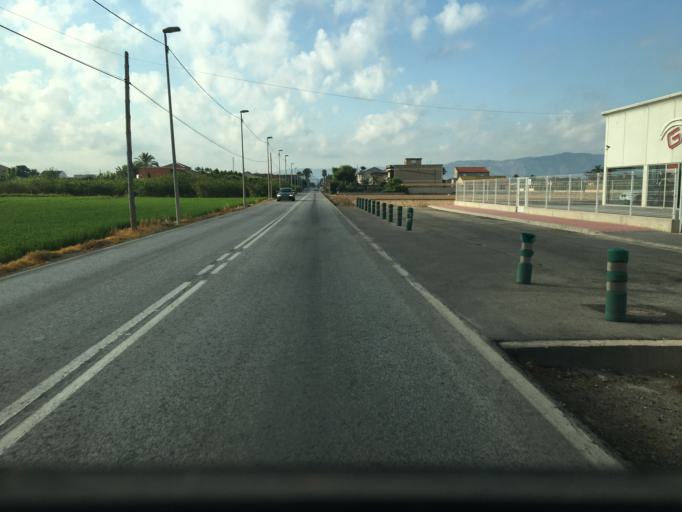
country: ES
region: Murcia
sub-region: Murcia
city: Santomera
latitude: 38.0371
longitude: -1.0454
